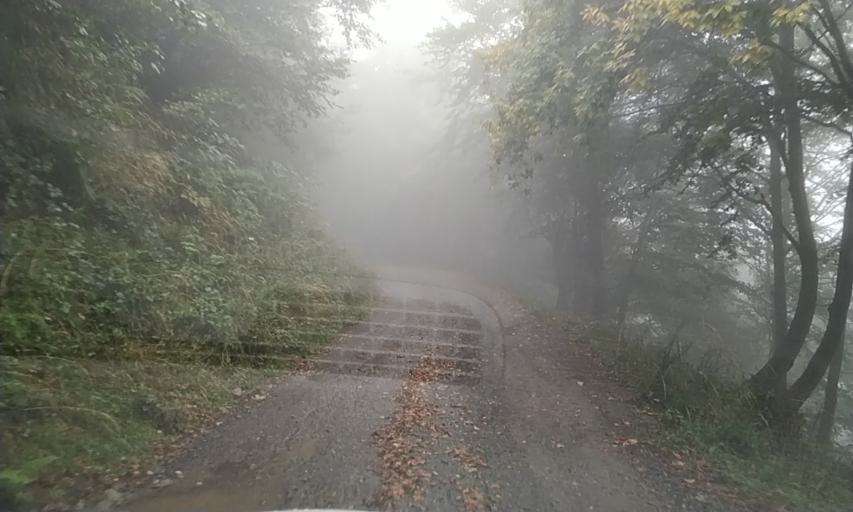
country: IT
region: Piedmont
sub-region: Provincia di Vercelli
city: Civiasco
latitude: 45.8363
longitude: 8.3215
